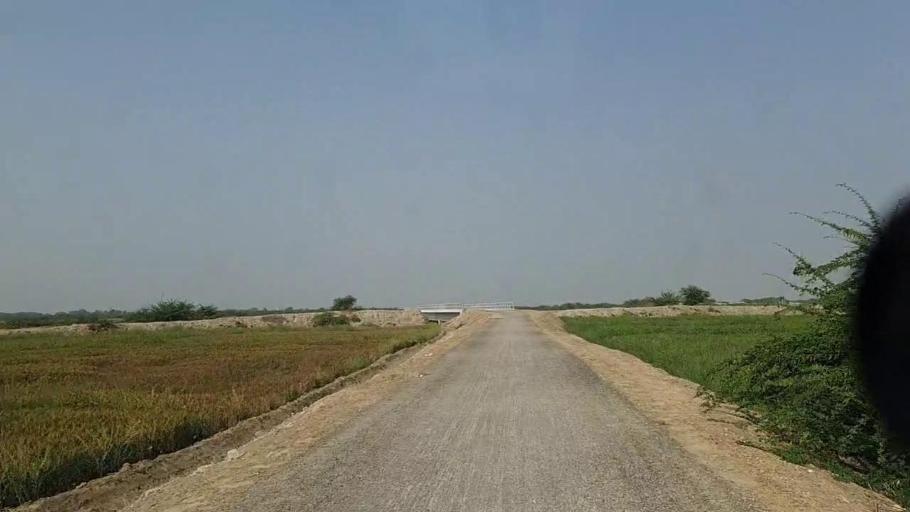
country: PK
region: Sindh
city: Naukot
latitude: 24.7779
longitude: 69.3096
